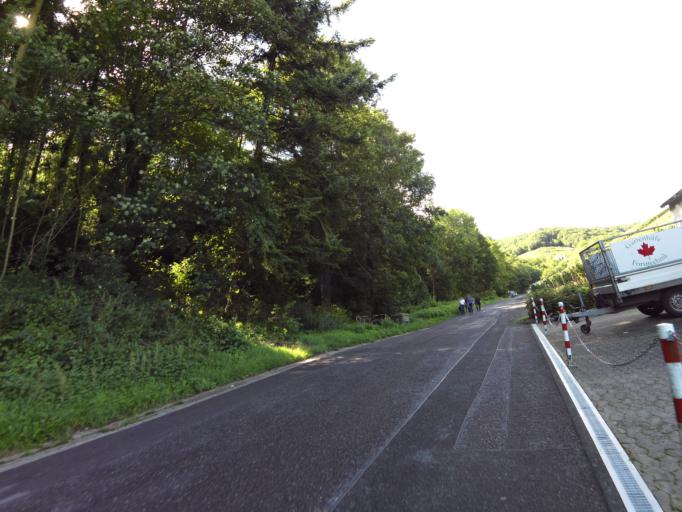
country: DE
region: Rheinland-Pfalz
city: Bad Neuenahr-Ahrweiler
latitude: 50.5391
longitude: 7.0837
